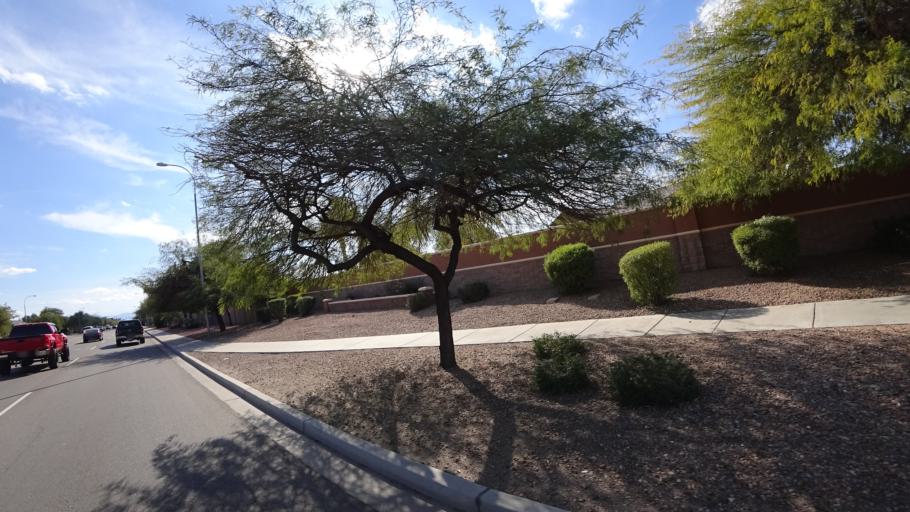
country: US
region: Arizona
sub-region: Maricopa County
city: Peoria
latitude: 33.6070
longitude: -112.2202
